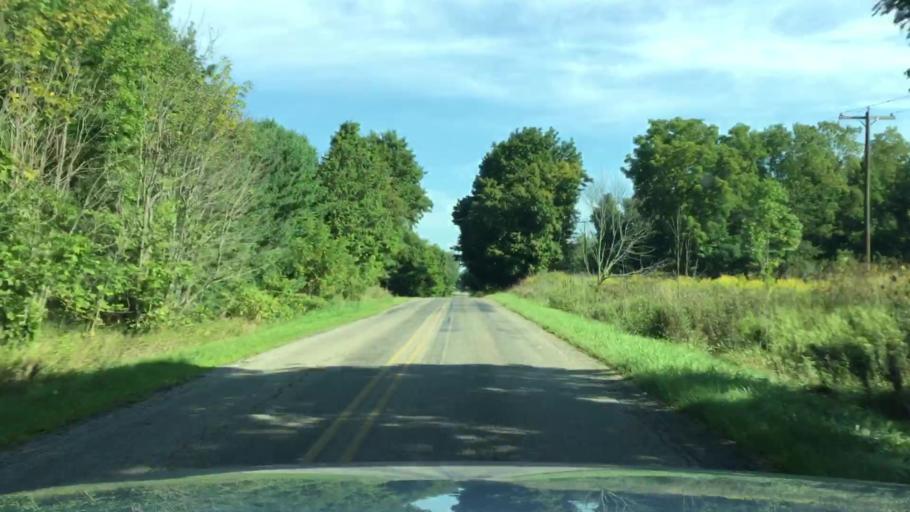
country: US
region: Michigan
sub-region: Lenawee County
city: Hudson
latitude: 41.8757
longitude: -84.4201
